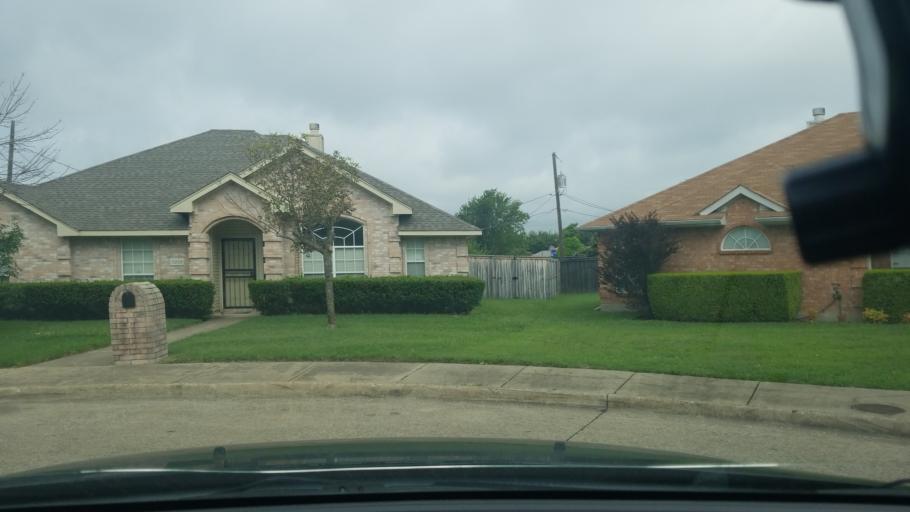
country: US
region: Texas
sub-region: Dallas County
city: Balch Springs
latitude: 32.7868
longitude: -96.6888
